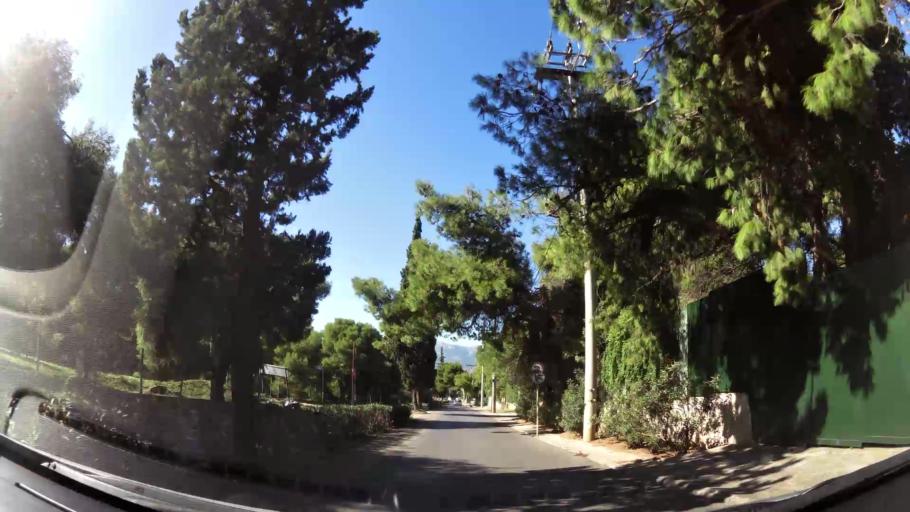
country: GR
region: Attica
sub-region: Nomarchia Athinas
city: Nea Erythraia
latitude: 38.0992
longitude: 23.8227
